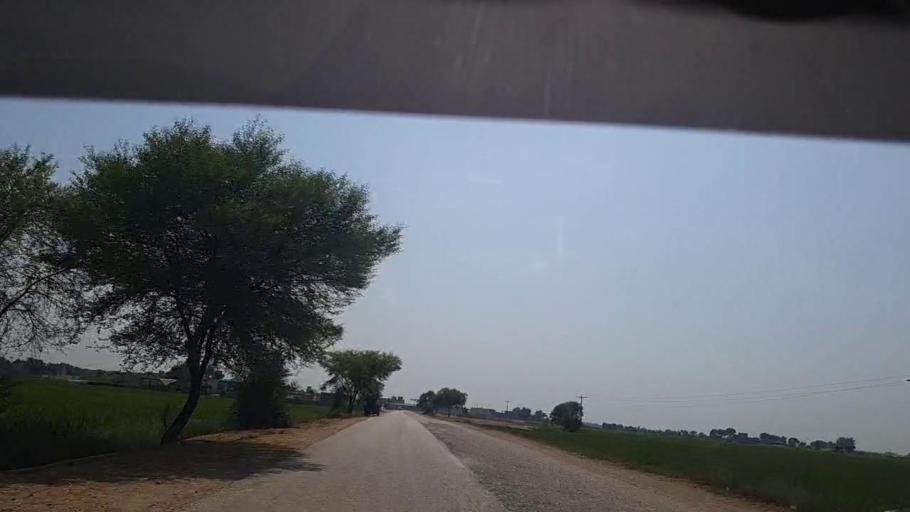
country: PK
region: Sindh
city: Thul
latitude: 28.1873
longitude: 68.7296
